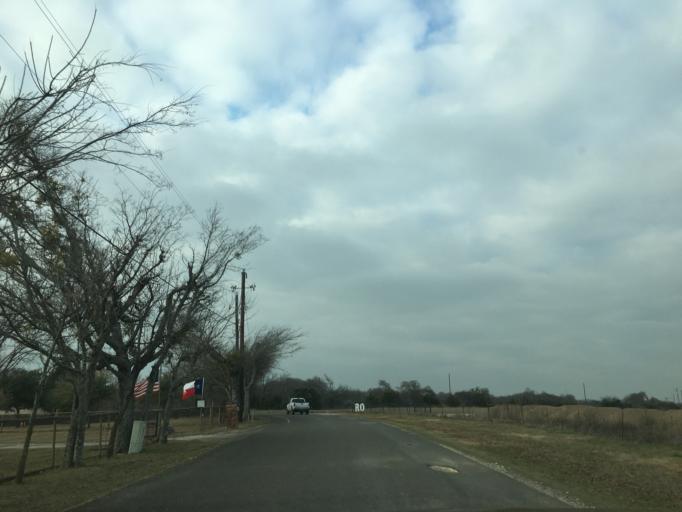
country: US
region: Texas
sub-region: Ellis County
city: Red Oak
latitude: 32.4933
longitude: -96.8030
